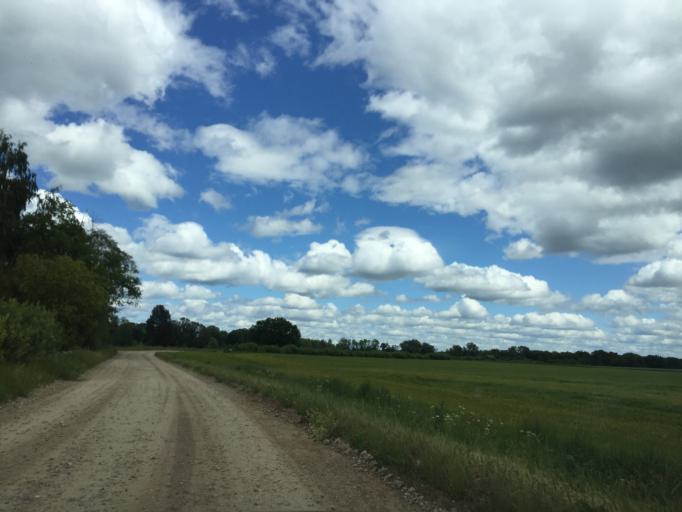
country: LV
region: Lecava
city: Iecava
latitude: 56.5877
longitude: 24.2396
